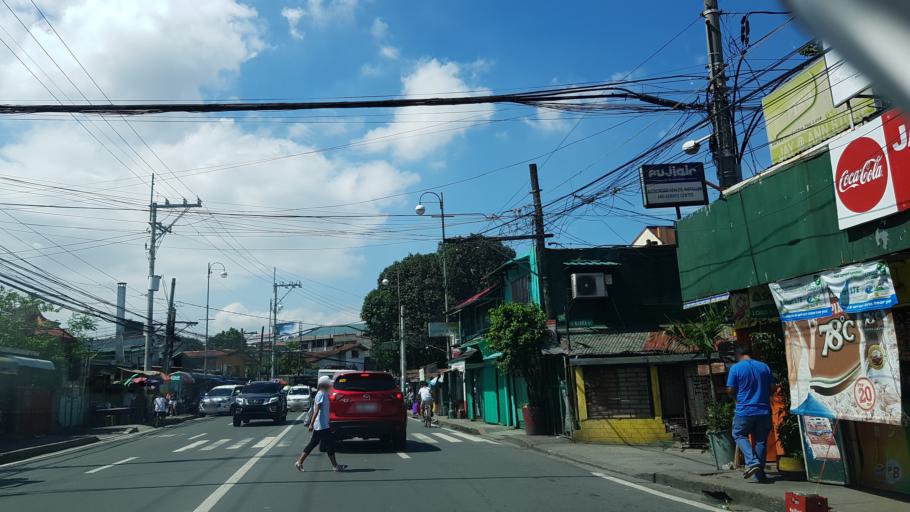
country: PH
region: Calabarzon
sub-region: Province of Rizal
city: Pateros
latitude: 14.5514
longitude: 121.0633
